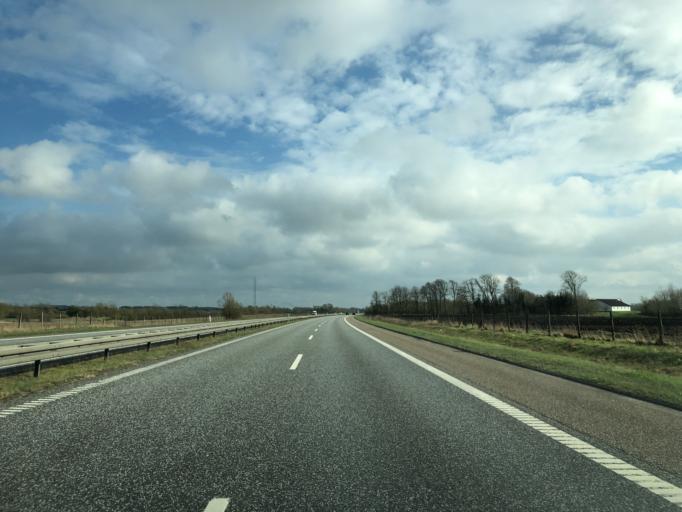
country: DK
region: North Denmark
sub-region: Alborg Kommune
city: Vestbjerg
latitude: 57.1557
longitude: 9.9453
